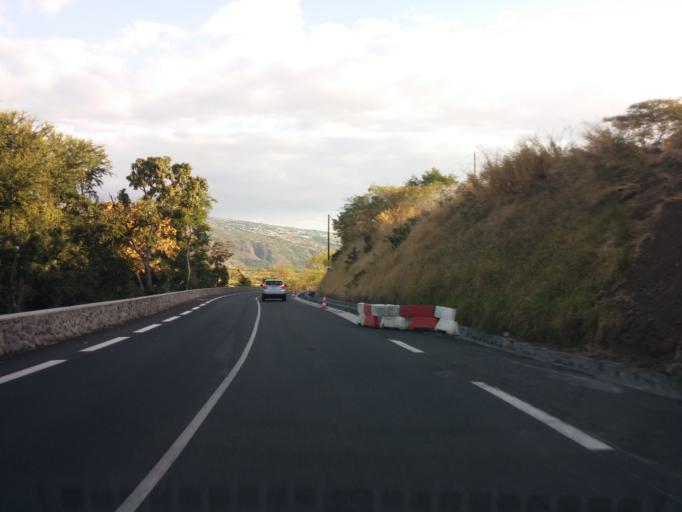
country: RE
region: Reunion
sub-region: Reunion
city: Le Port
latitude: -20.9701
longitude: 55.3092
